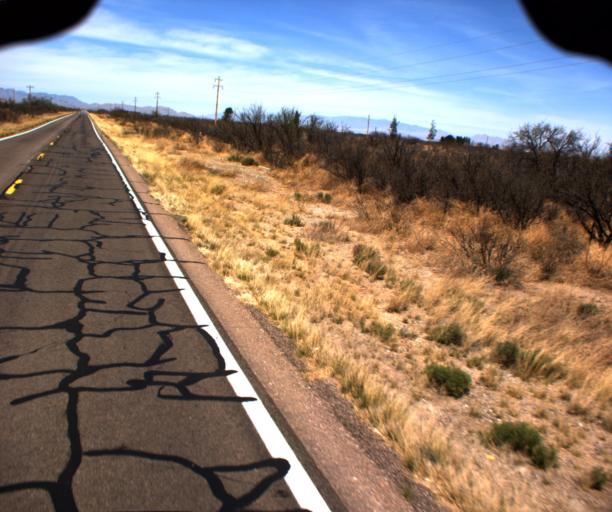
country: US
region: Arizona
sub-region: Cochise County
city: Willcox
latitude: 32.0698
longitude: -109.8960
